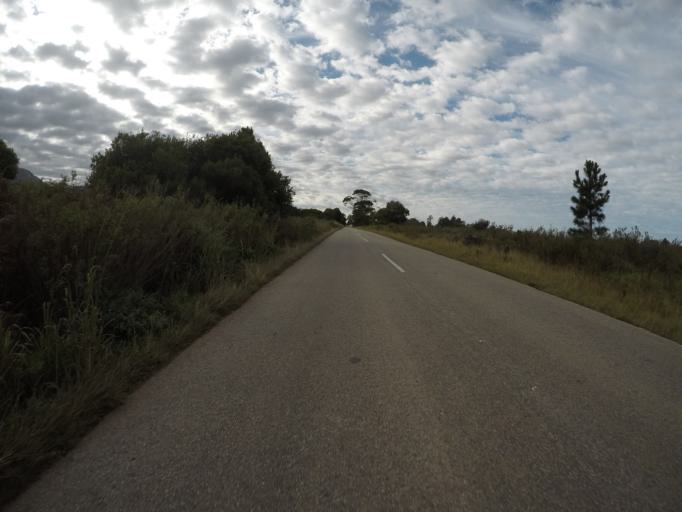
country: ZA
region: Eastern Cape
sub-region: Cacadu District Municipality
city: Kareedouw
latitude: -34.0439
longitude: 24.4313
